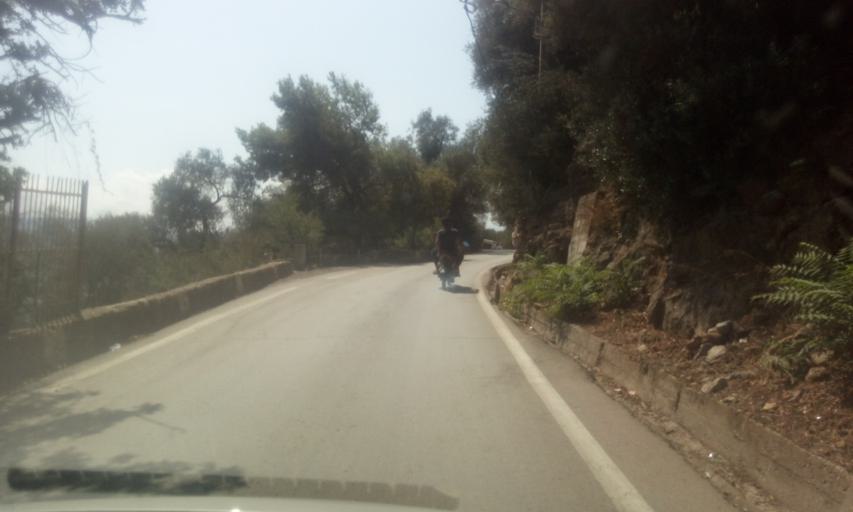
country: DZ
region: Bejaia
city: Bejaia
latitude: 36.7560
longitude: 5.0923
